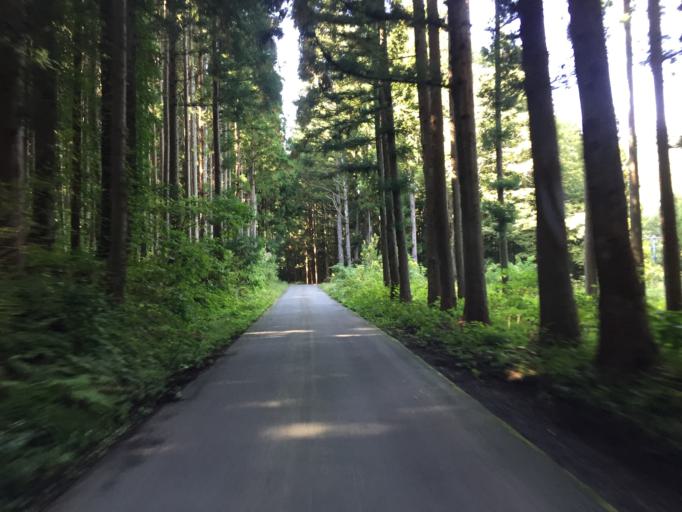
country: JP
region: Yamagata
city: Yonezawa
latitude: 37.8367
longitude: 140.2015
